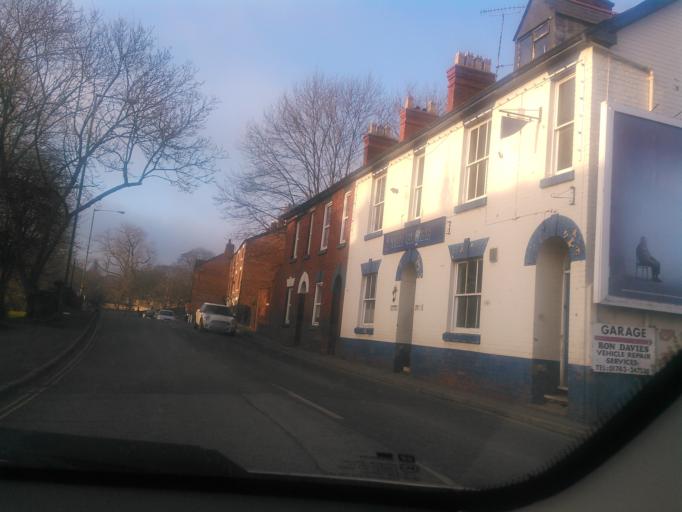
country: GB
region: England
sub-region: Shropshire
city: Shrewsbury
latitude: 52.7055
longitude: -2.7455
